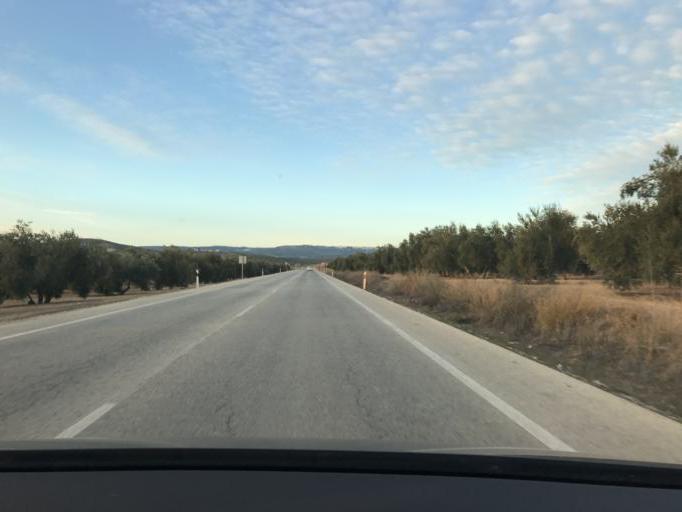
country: ES
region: Andalusia
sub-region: Provincia de Jaen
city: Ubeda
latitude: 37.9363
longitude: -3.3564
